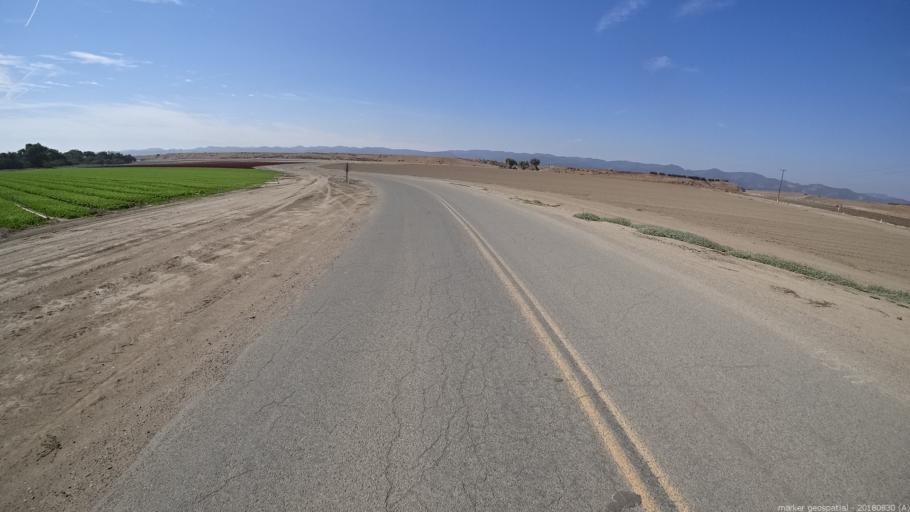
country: US
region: California
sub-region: Monterey County
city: King City
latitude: 36.1152
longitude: -121.0305
